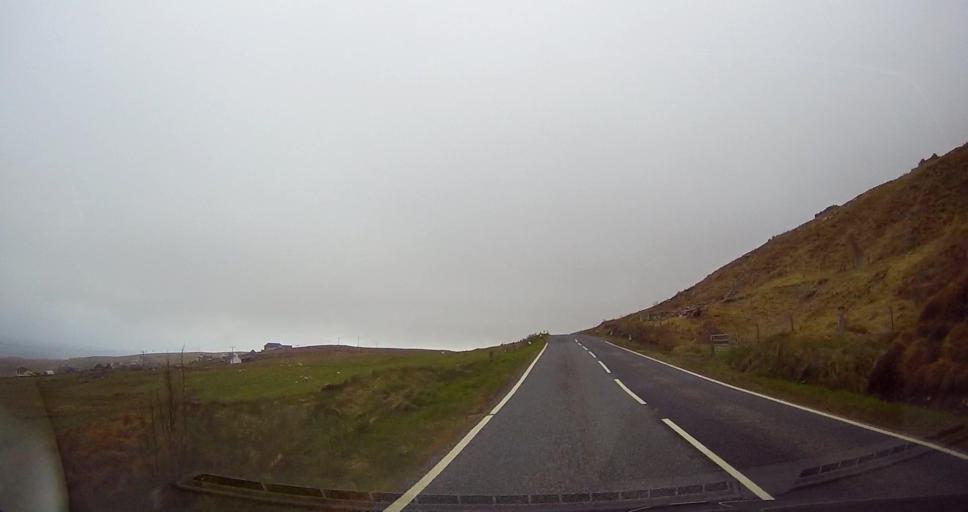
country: GB
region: Scotland
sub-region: Shetland Islands
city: Sandwick
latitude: 59.9718
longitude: -1.2781
